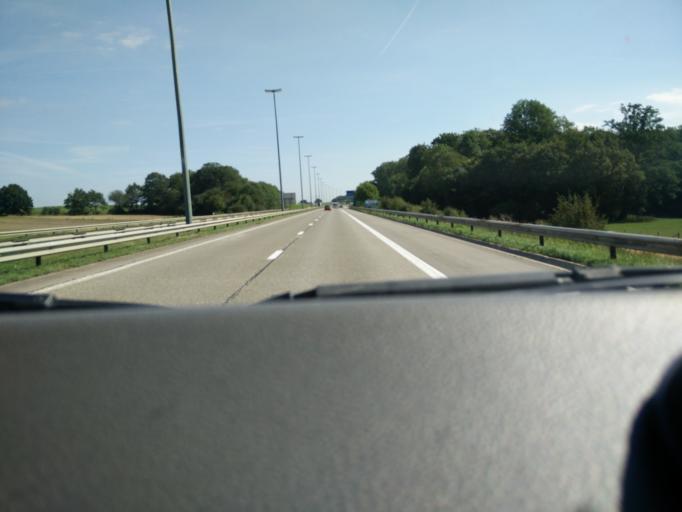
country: LU
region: Luxembourg
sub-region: Canton de Capellen
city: Clemency
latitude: 49.6393
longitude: 5.8747
